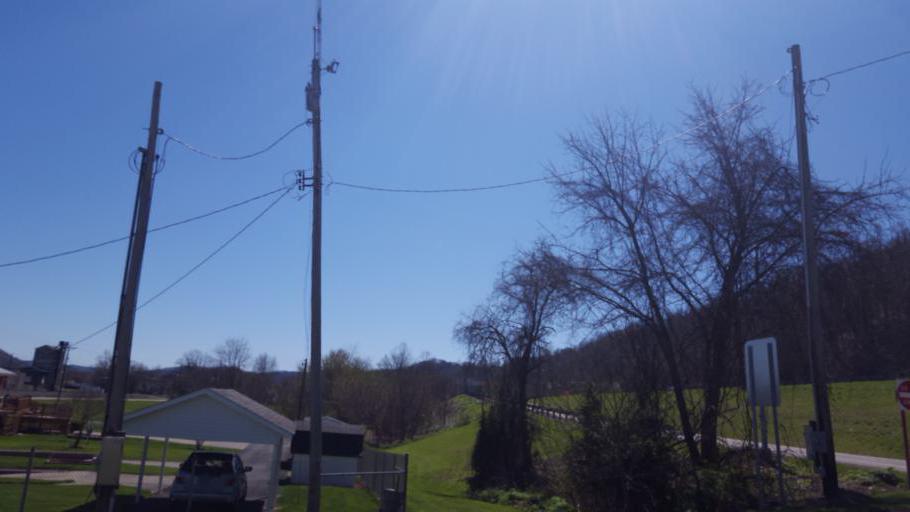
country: US
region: Ohio
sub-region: Jefferson County
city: Tiltonsville
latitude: 40.1741
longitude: -80.6984
